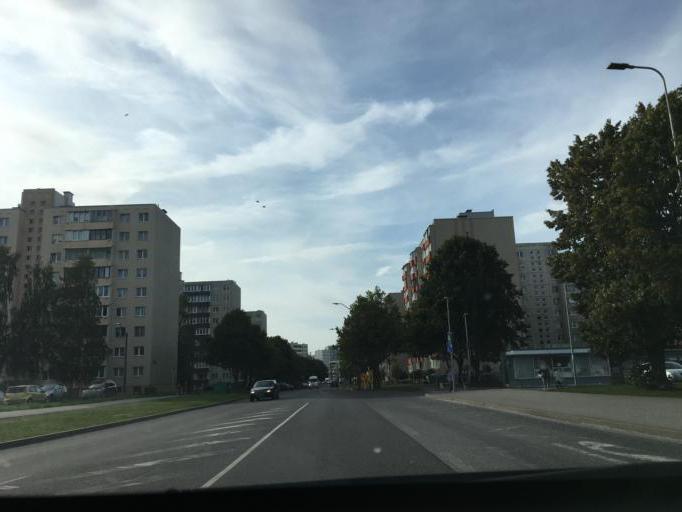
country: EE
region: Harju
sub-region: Tallinna linn
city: Kose
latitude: 59.4495
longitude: 24.8799
